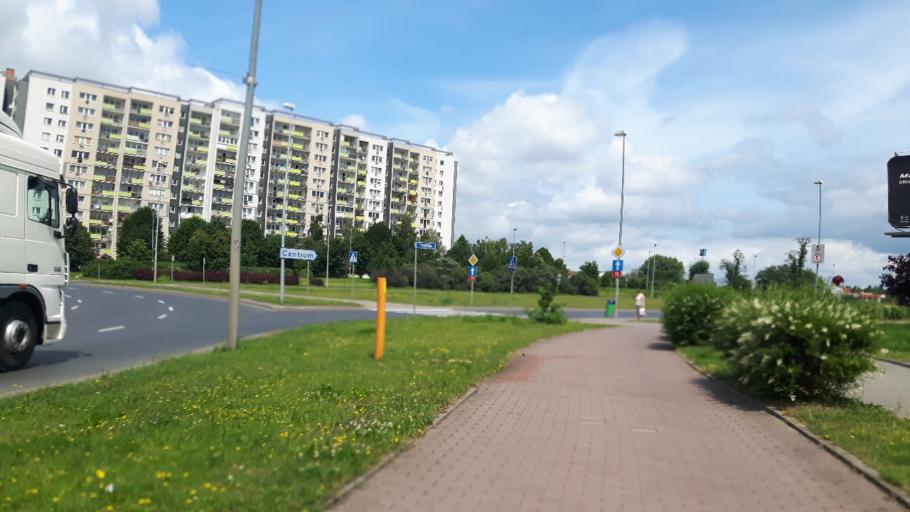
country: PL
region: West Pomeranian Voivodeship
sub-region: Powiat policki
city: Przeclaw
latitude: 53.4035
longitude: 14.5025
